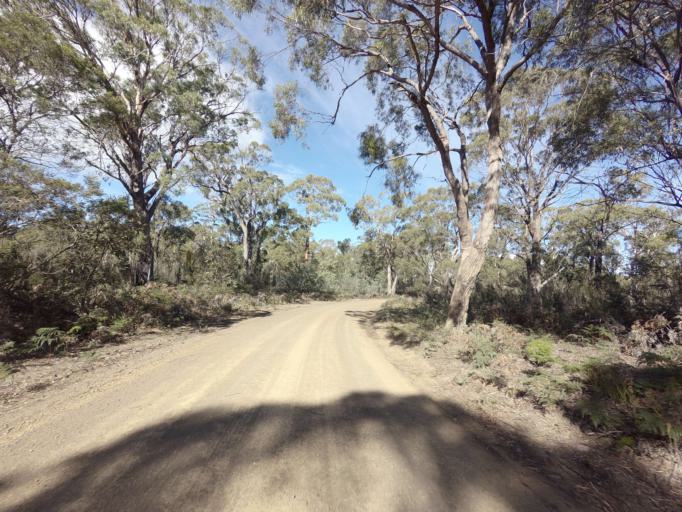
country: AU
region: Tasmania
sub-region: Clarence
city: Sandford
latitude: -42.9599
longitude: 147.7035
